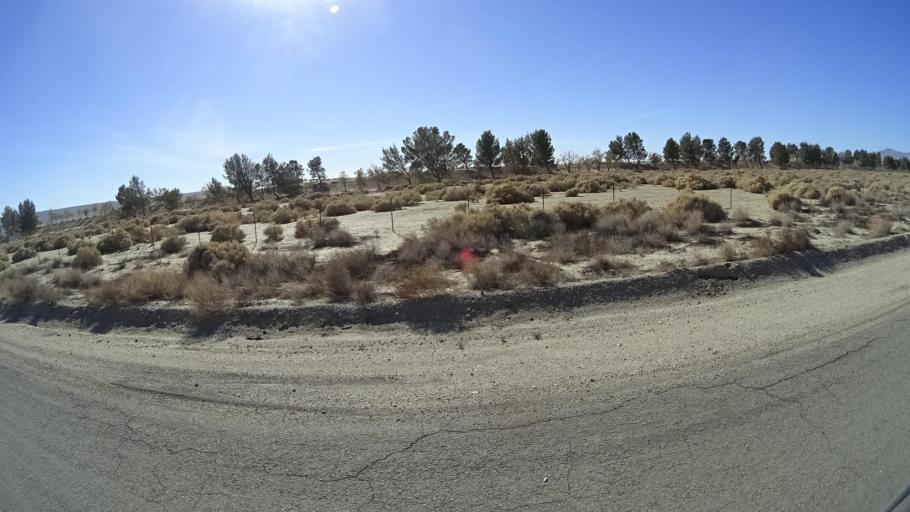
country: US
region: California
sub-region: Kern County
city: California City
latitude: 35.2869
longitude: -117.9532
